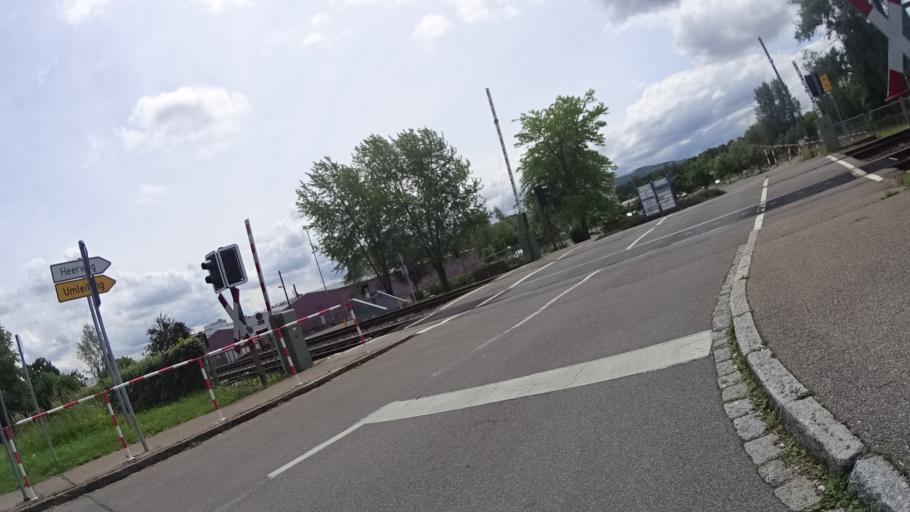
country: CH
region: Basel-City
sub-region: Basel-Stadt
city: Bettingen
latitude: 47.5524
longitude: 7.6527
